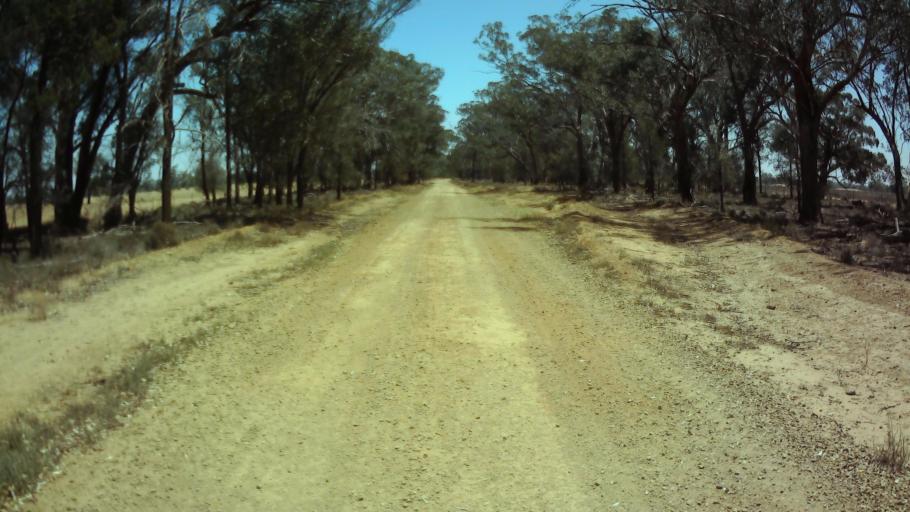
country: AU
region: New South Wales
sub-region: Weddin
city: Grenfell
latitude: -34.0382
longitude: 147.8528
